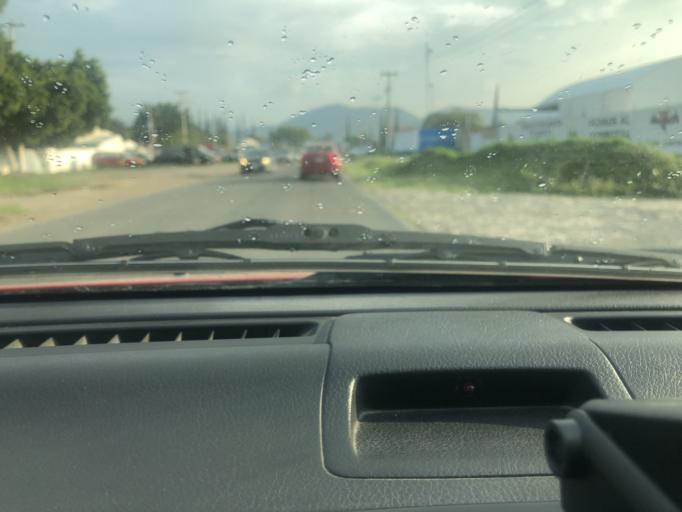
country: MX
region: Jalisco
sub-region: San Pedro Tlaquepaque
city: Santa Anita
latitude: 20.5543
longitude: -103.4185
